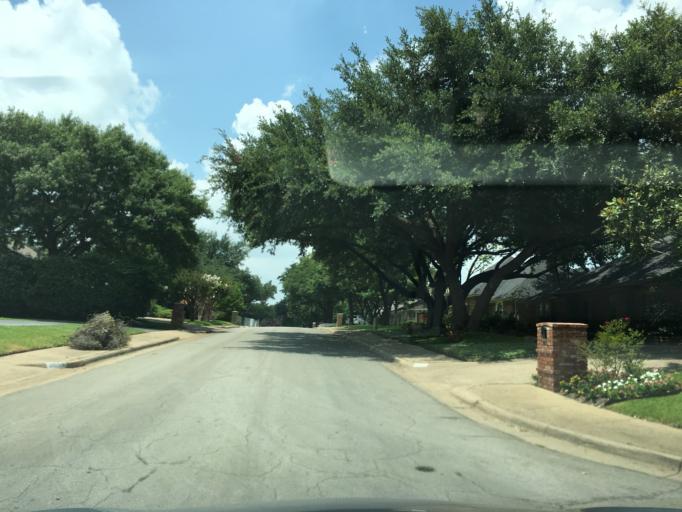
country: US
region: Texas
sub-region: Dallas County
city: University Park
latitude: 32.8912
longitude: -96.7819
